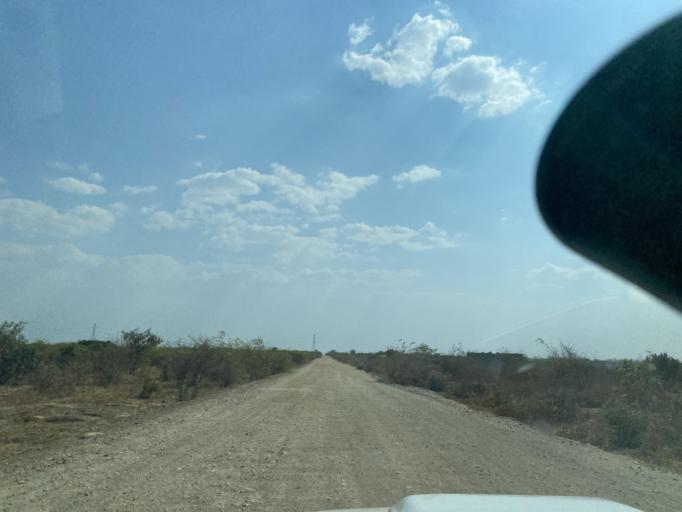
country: ZM
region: Lusaka
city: Lusaka
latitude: -15.3626
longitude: 28.0909
